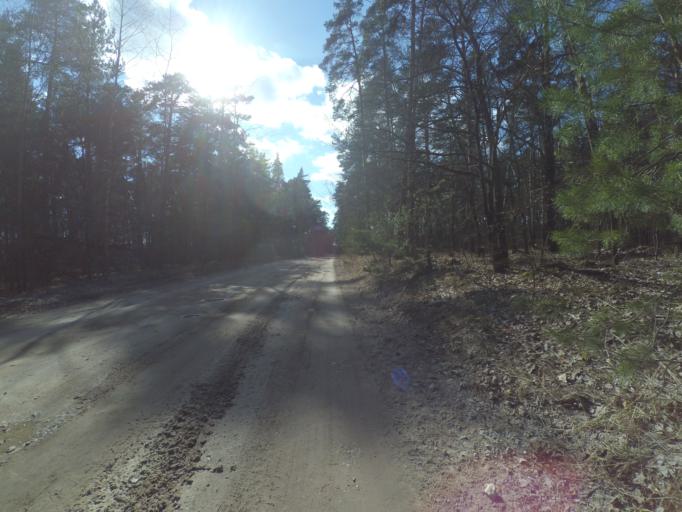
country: RU
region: Moskovskaya
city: Stupino
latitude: 54.8555
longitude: 37.9236
